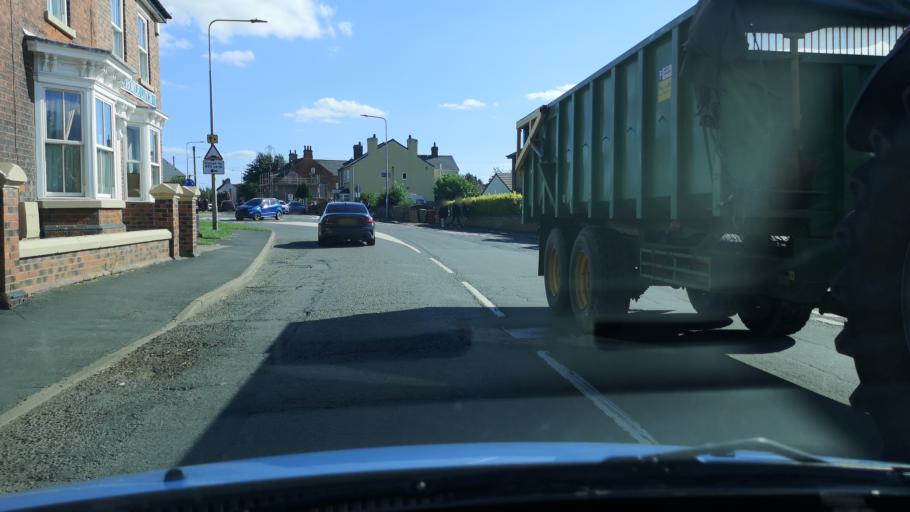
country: GB
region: England
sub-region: North Lincolnshire
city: Crowle
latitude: 53.6044
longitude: -0.8323
